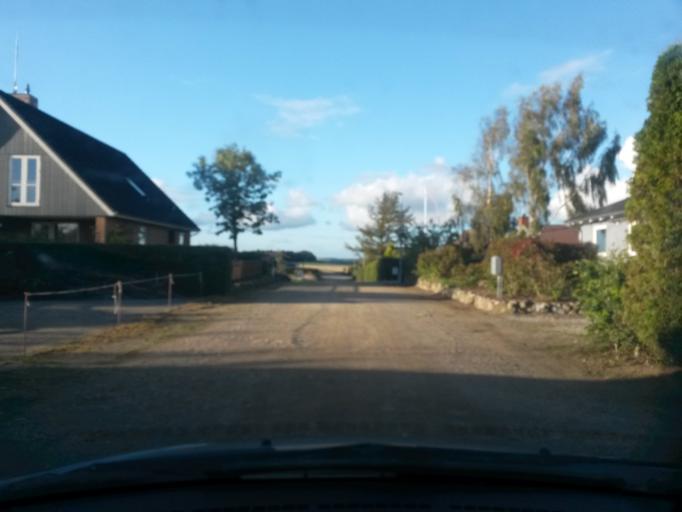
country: DK
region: Central Jutland
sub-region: Viborg Kommune
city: Viborg
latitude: 56.3758
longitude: 9.3916
